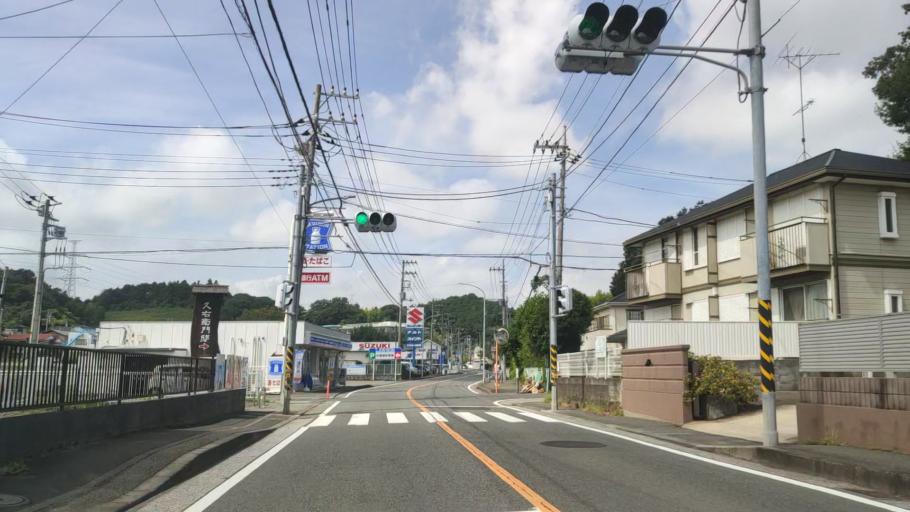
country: JP
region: Kanagawa
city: Minami-rinkan
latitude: 35.4315
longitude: 139.5336
